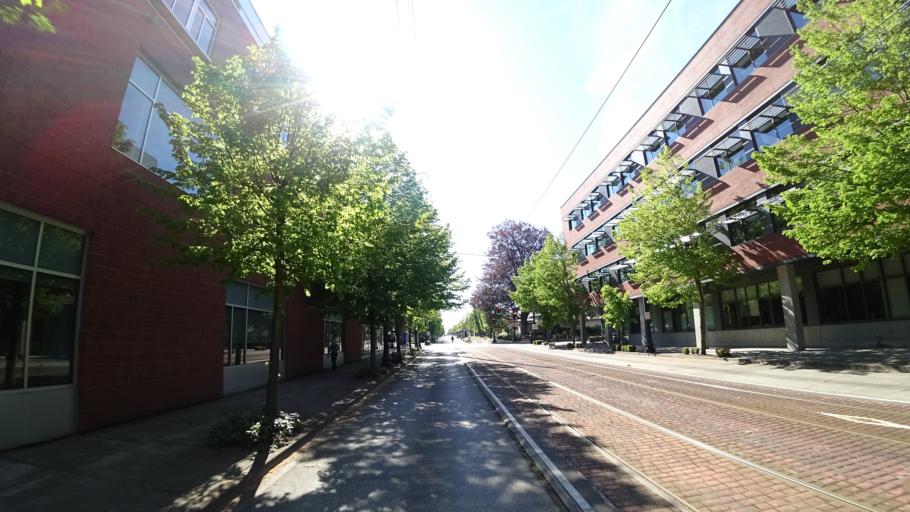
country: US
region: Oregon
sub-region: Washington County
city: Hillsboro
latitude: 45.5212
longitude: -122.9765
